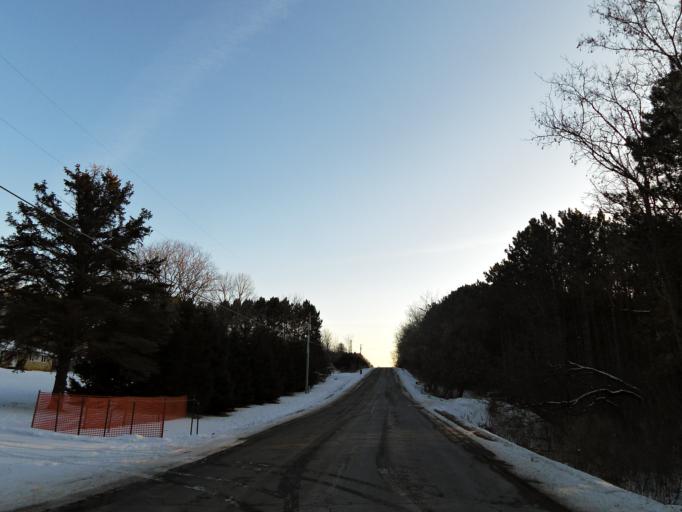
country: US
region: Wisconsin
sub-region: Saint Croix County
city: Hudson
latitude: 44.9591
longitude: -92.6803
